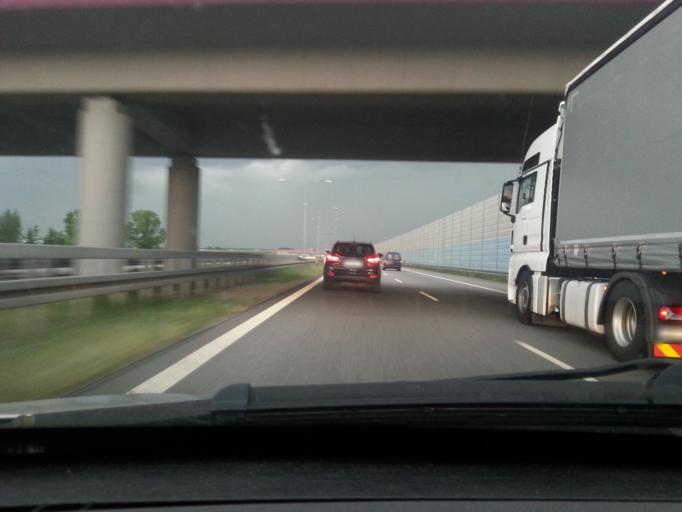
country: PL
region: Lodz Voivodeship
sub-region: powiat Lowicki
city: Lyszkowice
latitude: 51.9919
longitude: 19.9059
